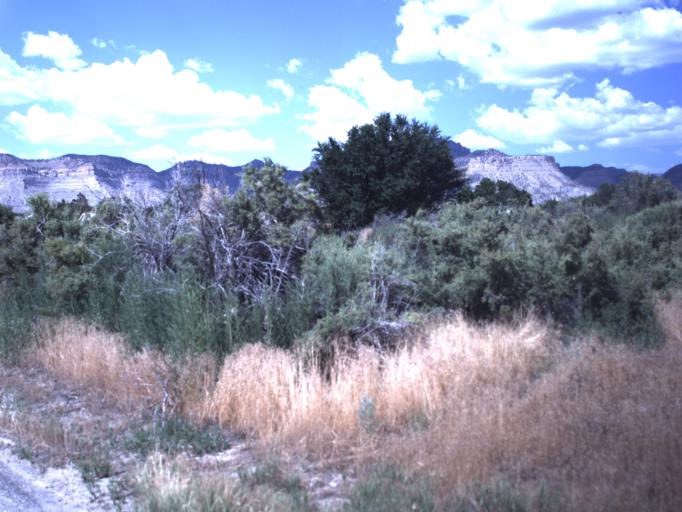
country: US
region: Utah
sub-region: Carbon County
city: Spring Glen
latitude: 39.6573
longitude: -110.8560
